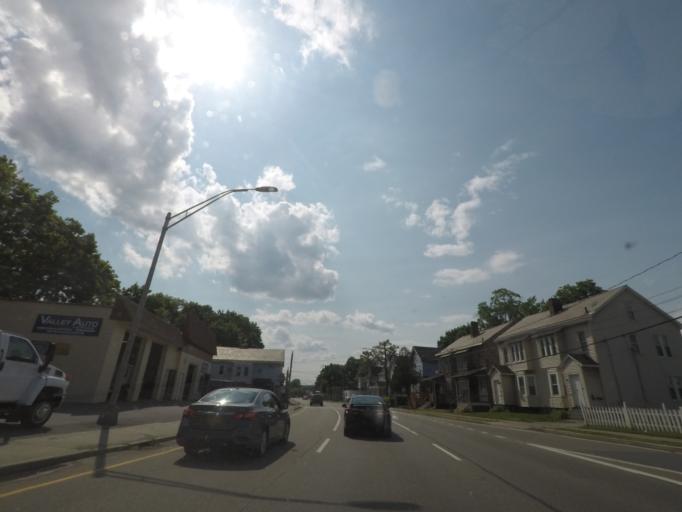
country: US
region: New York
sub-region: Dutchess County
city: Poughkeepsie
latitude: 41.7021
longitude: -73.9169
